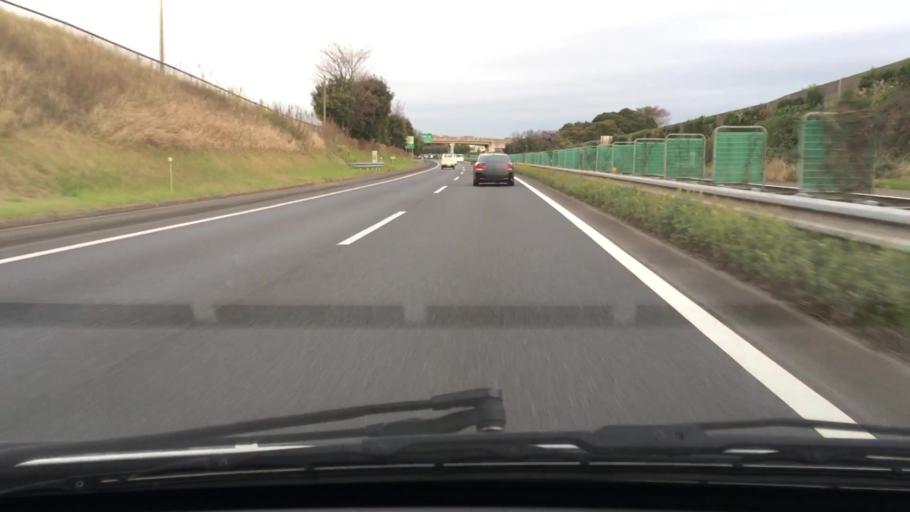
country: JP
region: Chiba
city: Ichihara
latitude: 35.4249
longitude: 140.0325
